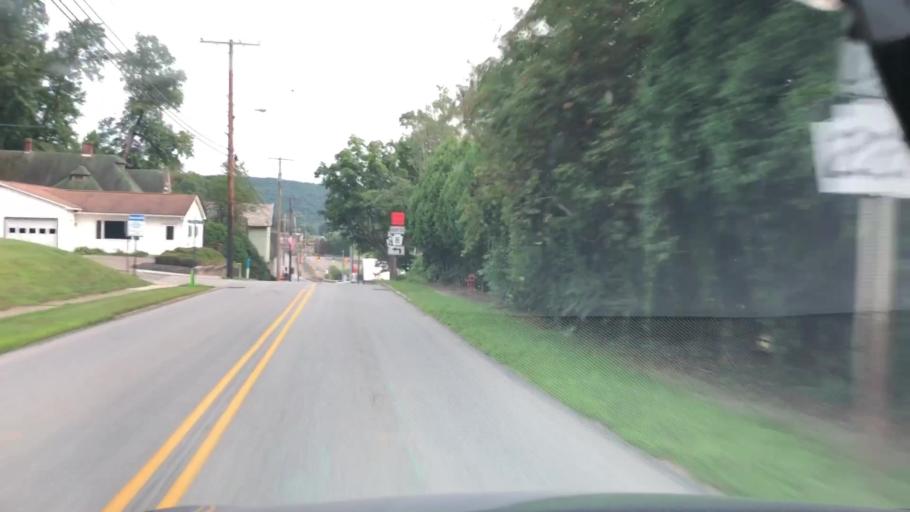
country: US
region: Pennsylvania
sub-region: Venango County
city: Hasson Heights
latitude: 41.4706
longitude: -79.6920
